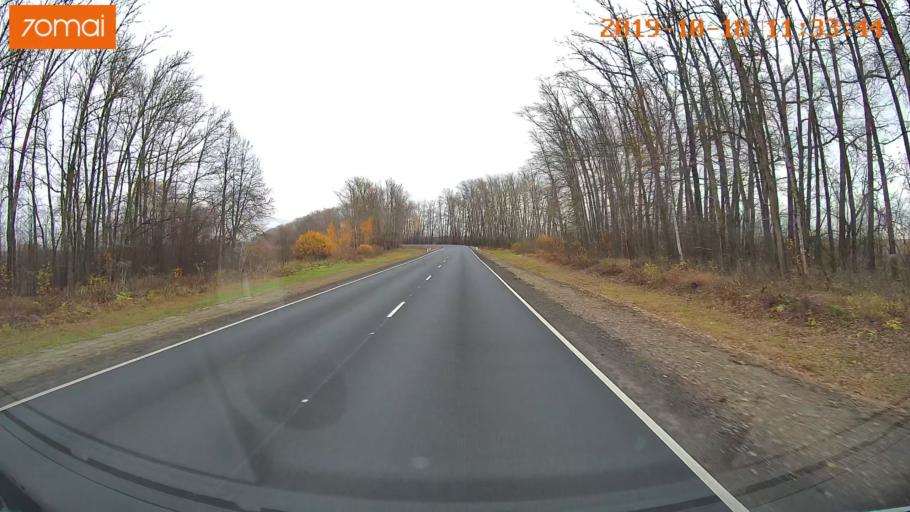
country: RU
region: Rjazan
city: Oktyabr'skiy
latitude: 54.1387
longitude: 38.7474
